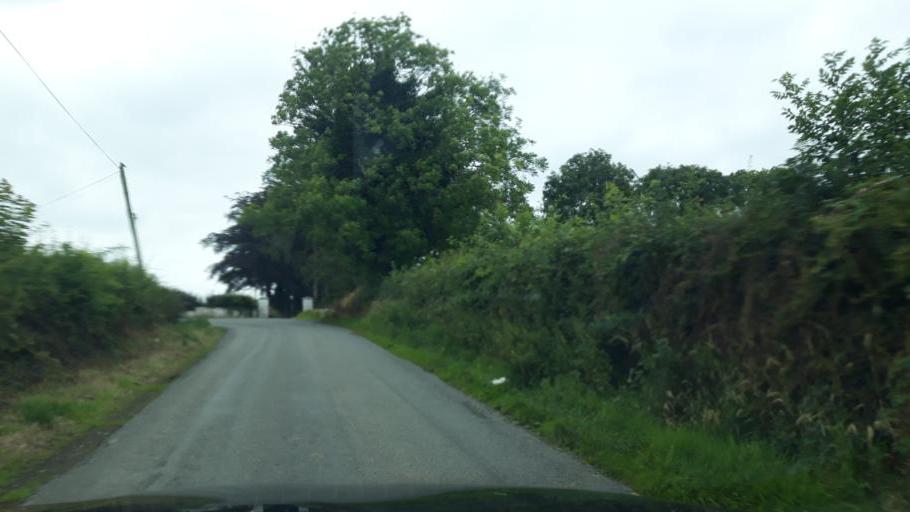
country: IE
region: Leinster
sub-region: Kilkenny
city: Ballyragget
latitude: 52.6990
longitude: -7.4137
